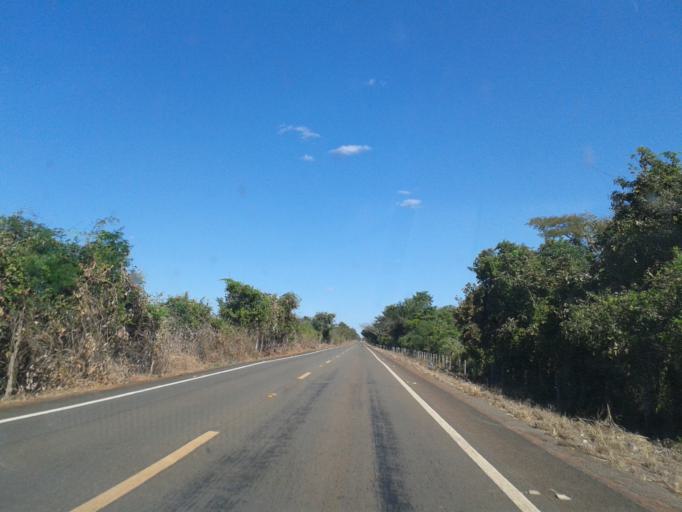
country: BR
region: Goias
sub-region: Sao Miguel Do Araguaia
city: Sao Miguel do Araguaia
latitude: -13.8958
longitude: -50.3275
